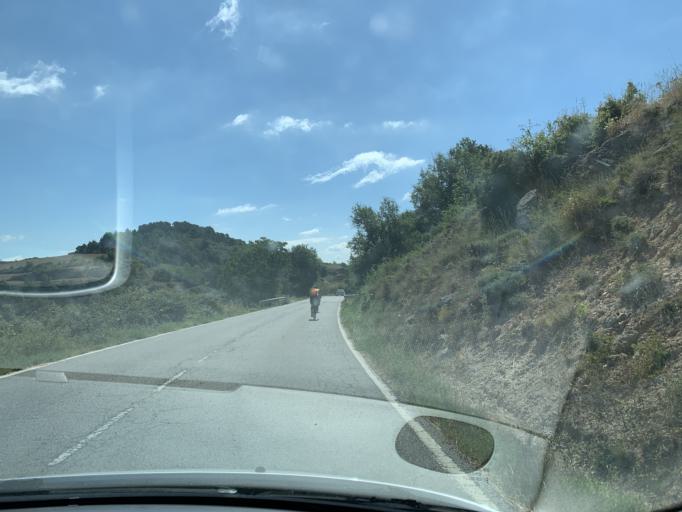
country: ES
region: Catalonia
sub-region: Provincia de Tarragona
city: Santa Coloma de Queralt
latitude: 41.5428
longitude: 1.3696
